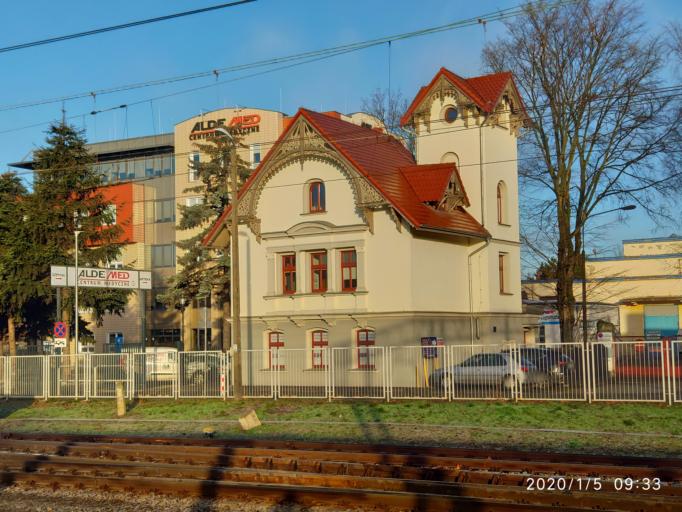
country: PL
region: Lubusz
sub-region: Zielona Gora
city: Zielona Gora
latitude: 51.9474
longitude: 15.5153
